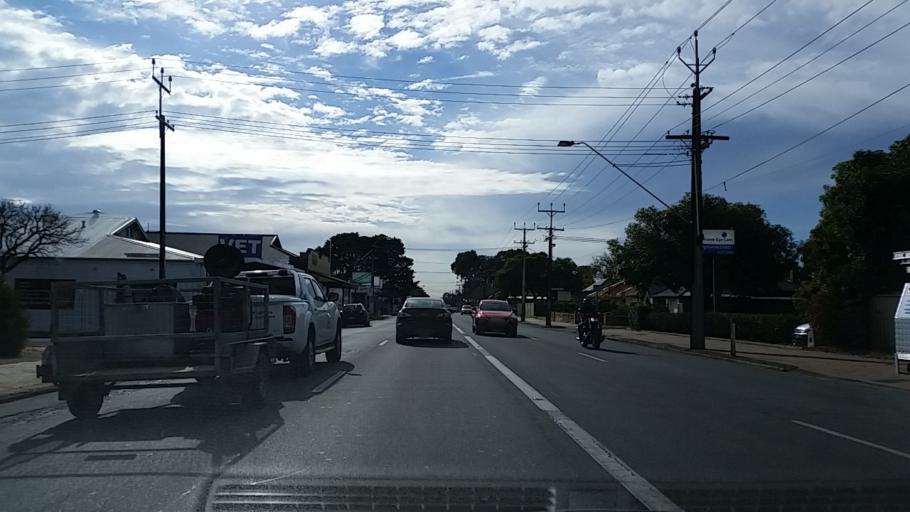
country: AU
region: South Australia
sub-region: Mitcham
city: Clarence Gardens
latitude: -34.9735
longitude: 138.5913
